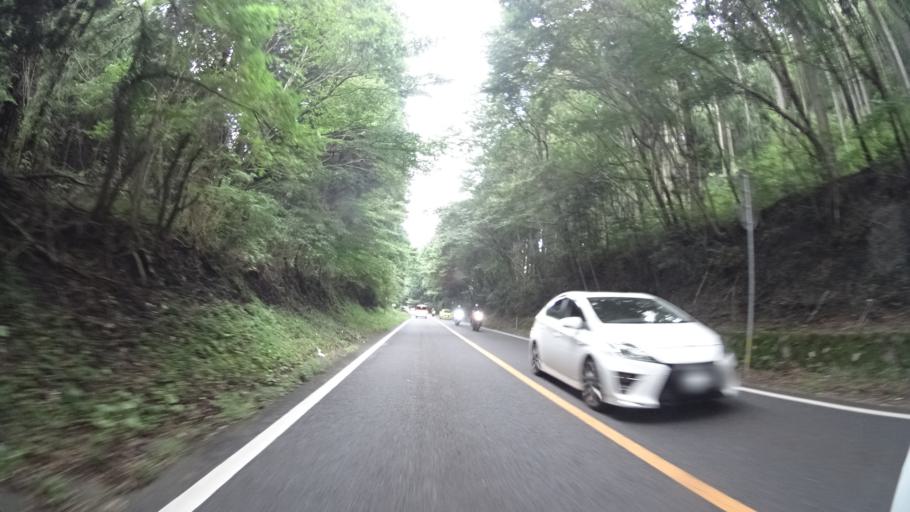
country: JP
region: Oita
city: Tsukawaki
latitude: 33.1931
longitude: 131.2737
